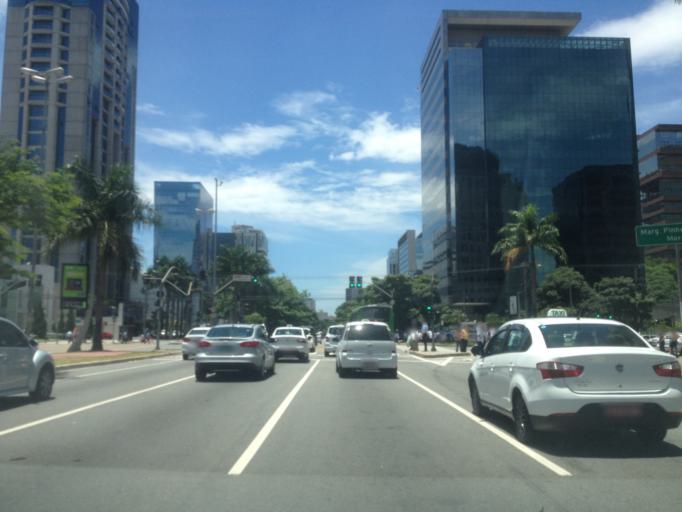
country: BR
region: Sao Paulo
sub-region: Sao Paulo
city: Sao Paulo
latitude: -23.5896
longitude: -46.6817
